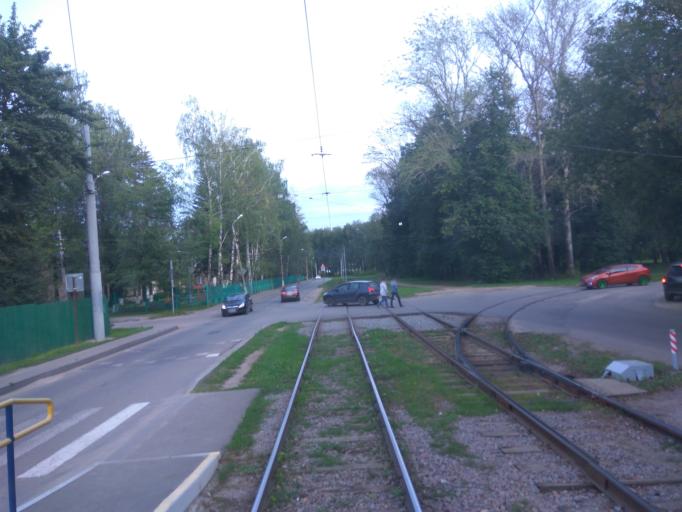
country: RU
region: Moskovskaya
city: Kolomna
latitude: 55.0745
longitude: 38.7841
